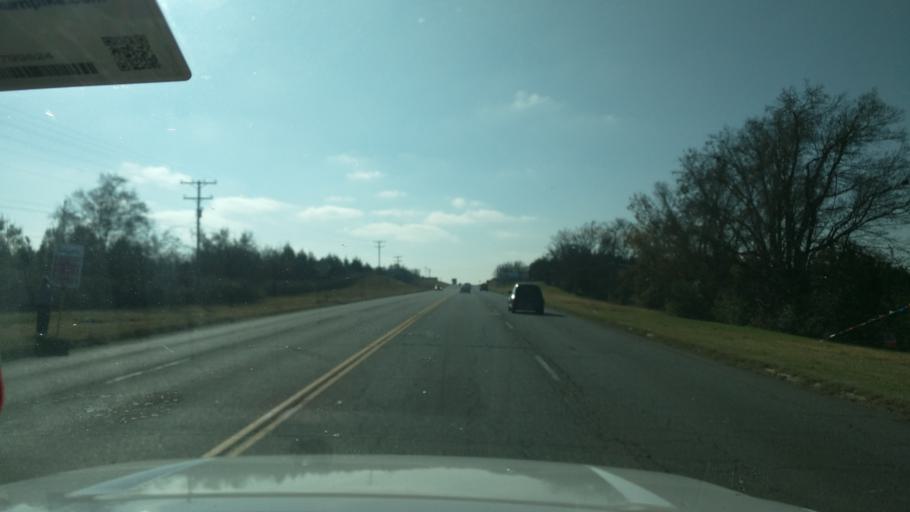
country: US
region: Oklahoma
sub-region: Washington County
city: Bartlesville
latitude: 36.6904
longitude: -95.9352
